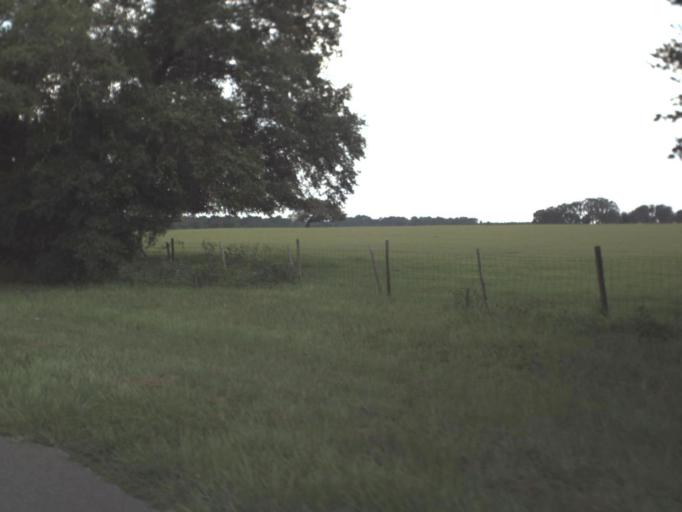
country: US
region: Florida
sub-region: Hillsborough County
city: Balm
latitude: 27.7047
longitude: -82.1904
